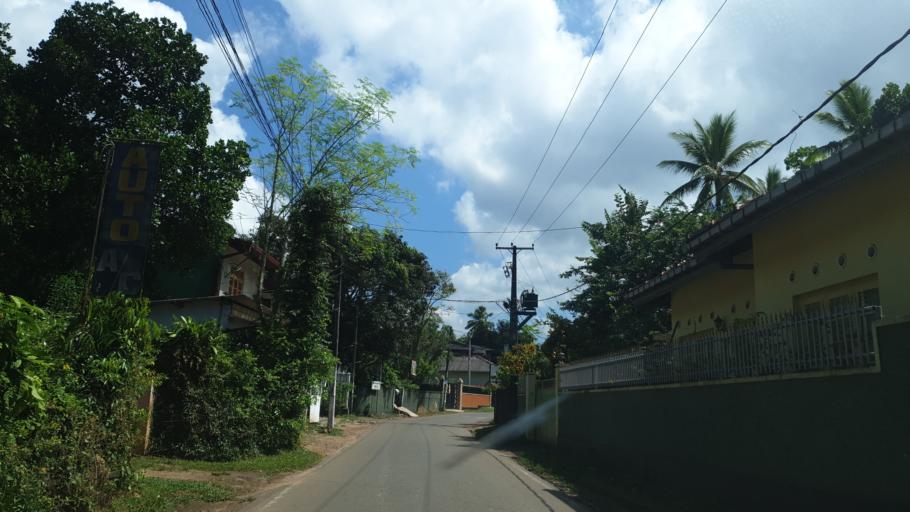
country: LK
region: Western
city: Panadura
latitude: 6.6742
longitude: 79.9383
